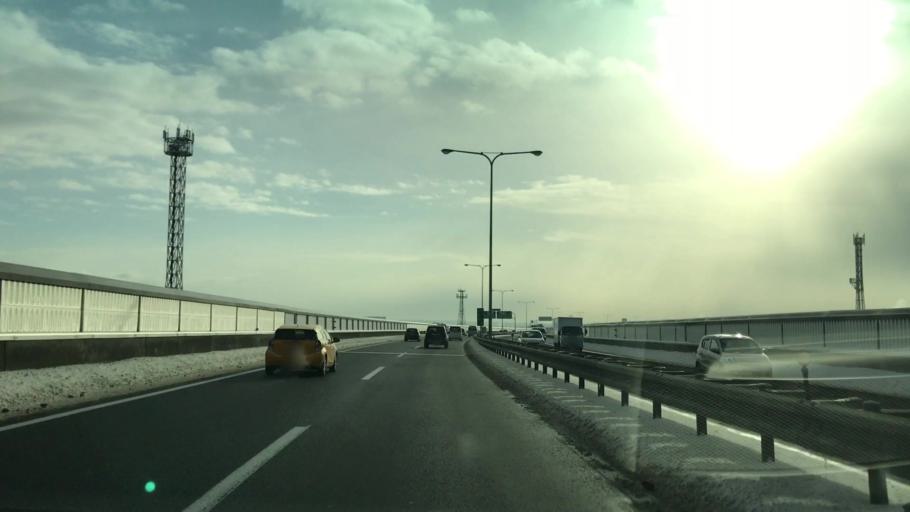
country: JP
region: Hokkaido
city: Sapporo
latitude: 43.0893
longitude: 141.4129
